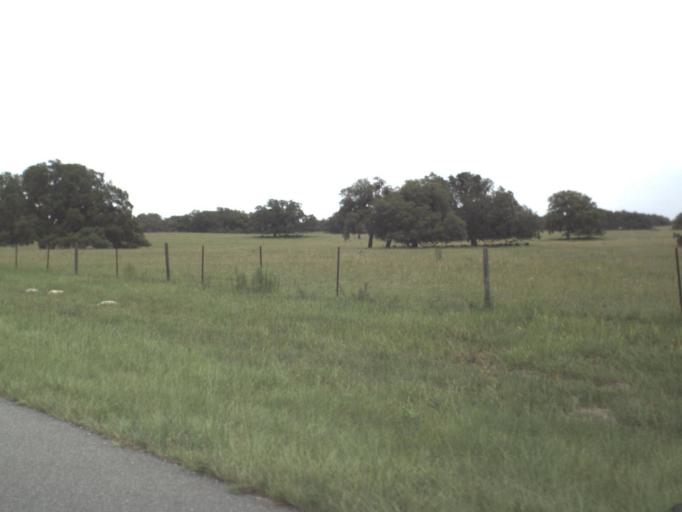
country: US
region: Florida
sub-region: Hernando County
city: Ridge Manor
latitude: 28.5032
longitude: -82.1715
